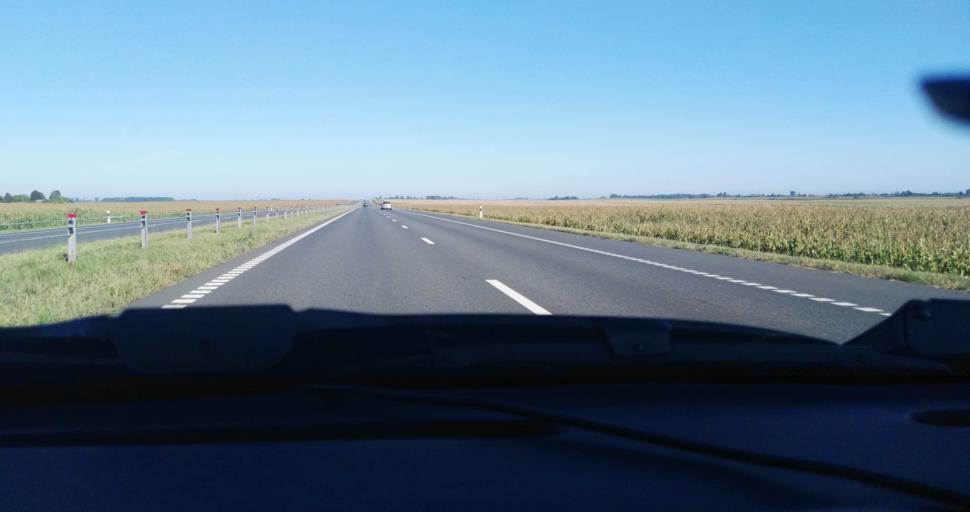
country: BY
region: Gomel
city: Buda-Kashalyova
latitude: 52.5259
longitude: 30.6159
